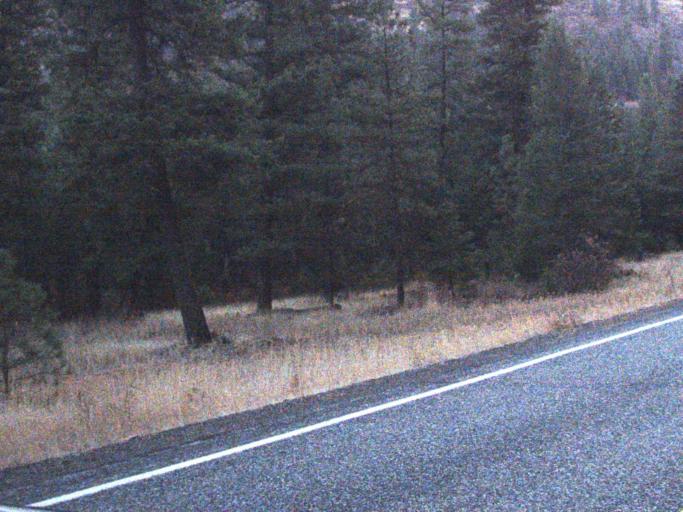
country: US
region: Washington
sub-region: Ferry County
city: Republic
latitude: 48.3625
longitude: -118.7417
